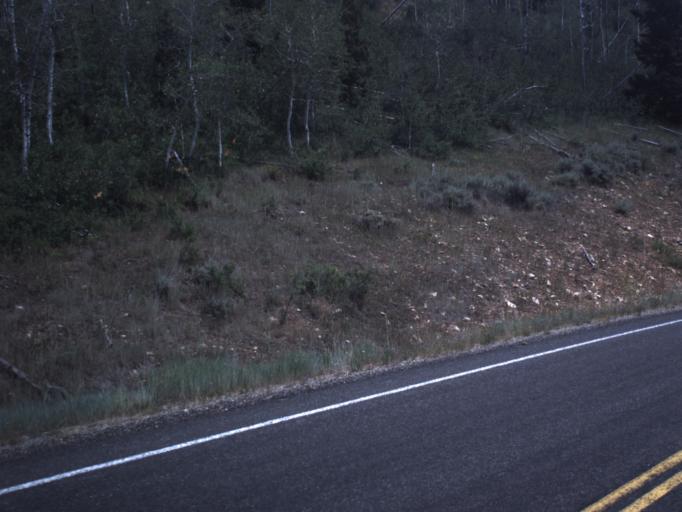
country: US
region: Utah
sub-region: Summit County
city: Francis
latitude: 40.4769
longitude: -110.9331
